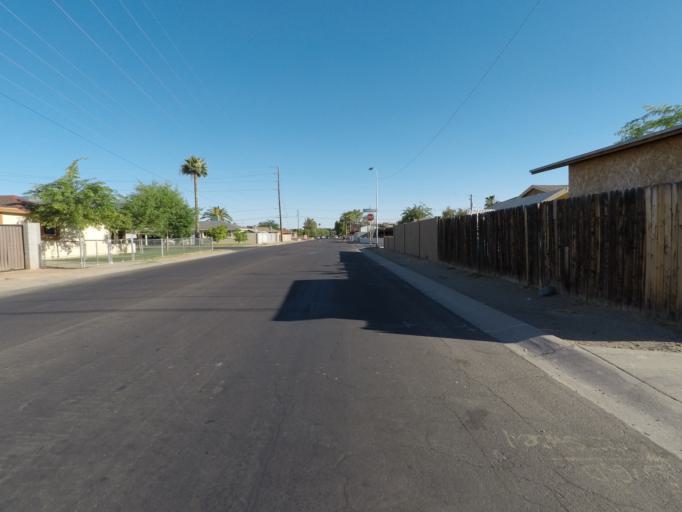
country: US
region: Arizona
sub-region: Maricopa County
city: Glendale
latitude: 33.5207
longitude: -112.1300
